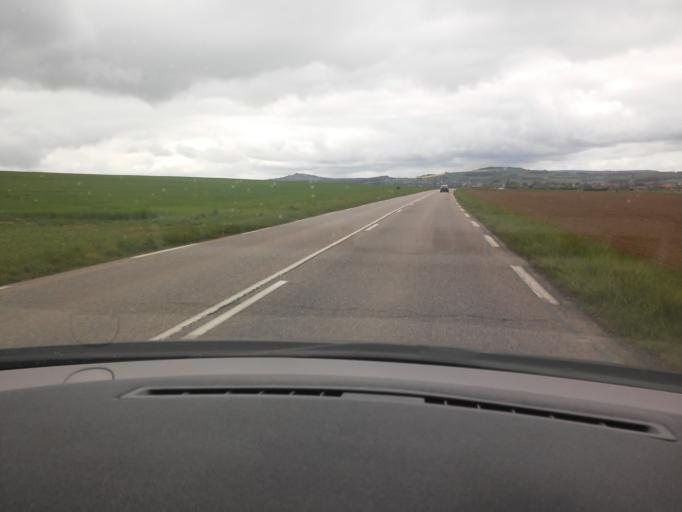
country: FR
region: Lorraine
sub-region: Departement de la Moselle
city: Verny
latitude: 48.9496
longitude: 6.1608
